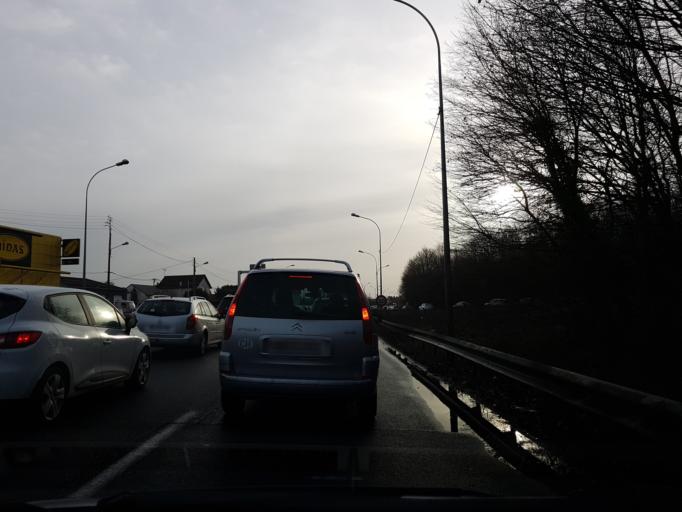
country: FR
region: Ile-de-France
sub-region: Departement de l'Essonne
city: Brunoy
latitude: 48.6874
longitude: 2.4850
